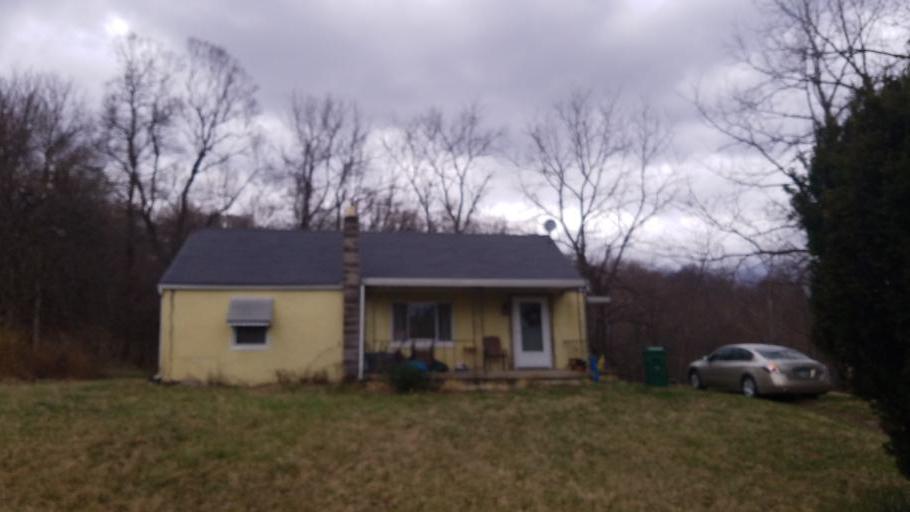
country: US
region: Ohio
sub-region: Licking County
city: Newark
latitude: 40.1486
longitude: -82.2776
